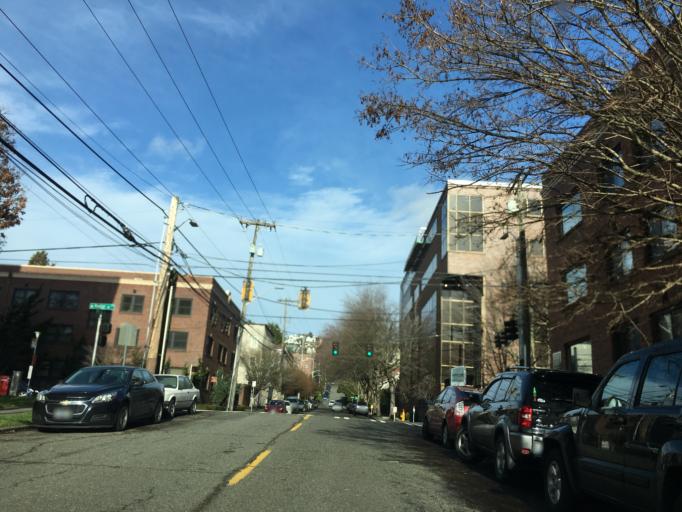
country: US
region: Washington
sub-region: King County
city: Seattle
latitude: 47.6243
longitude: -122.3606
